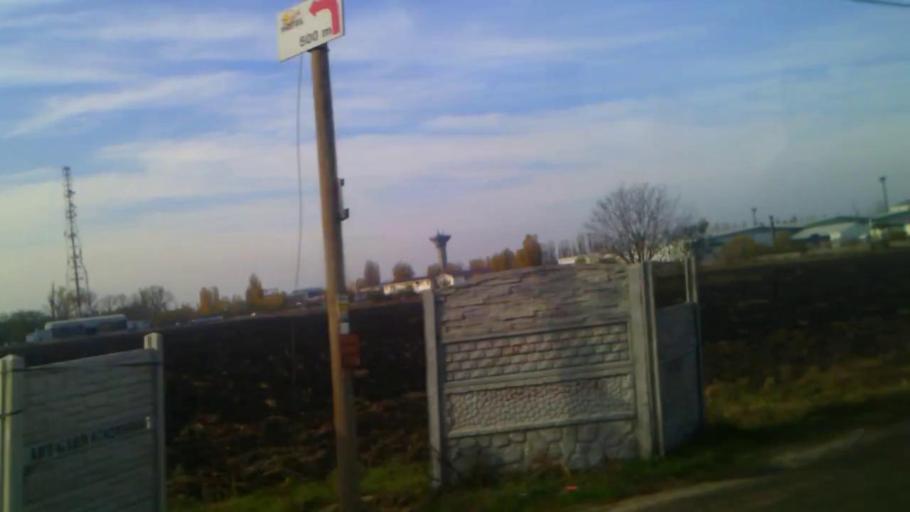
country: RO
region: Ilfov
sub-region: Comuna Berceni
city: Berceni
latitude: 44.3390
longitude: 26.1660
